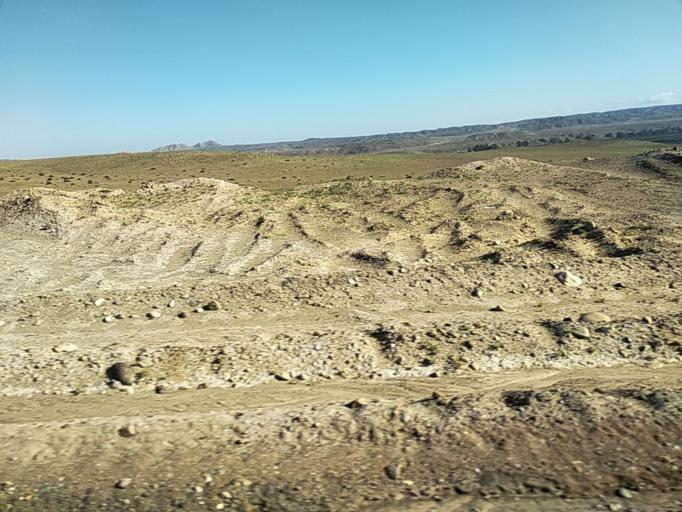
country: CL
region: Atacama
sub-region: Provincia de Copiapo
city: Copiapo
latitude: -27.3277
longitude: -70.7732
